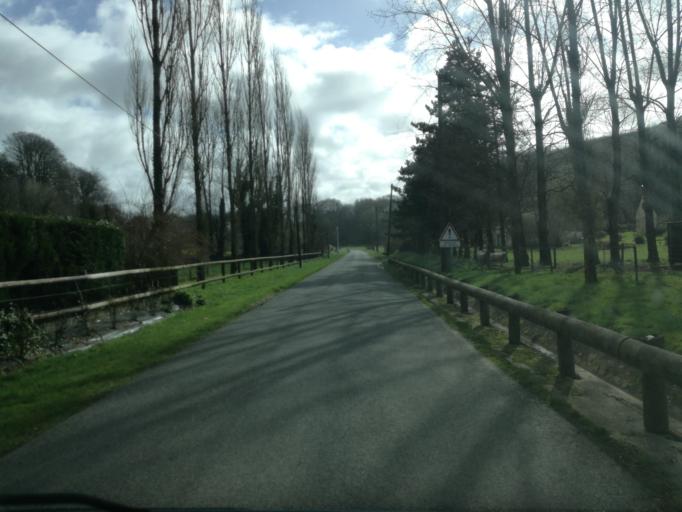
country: FR
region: Haute-Normandie
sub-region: Departement de la Seine-Maritime
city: Bretteville-du-Grand-Caux
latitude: 49.6993
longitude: 0.4604
